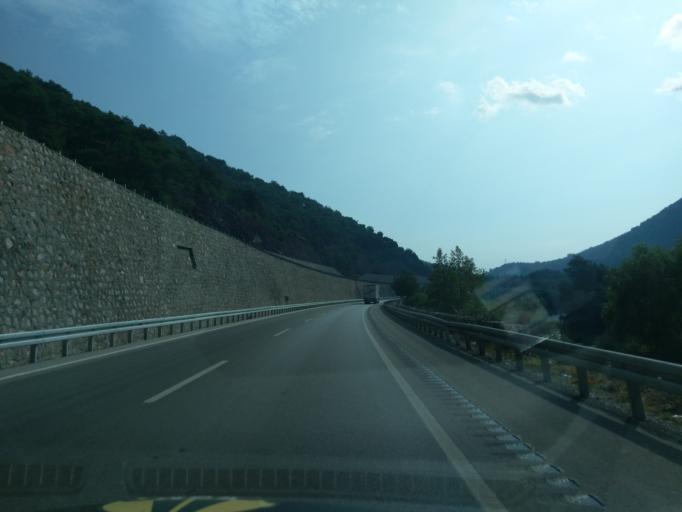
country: TR
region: Amasya
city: Akdag
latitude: 40.7539
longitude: 36.0684
